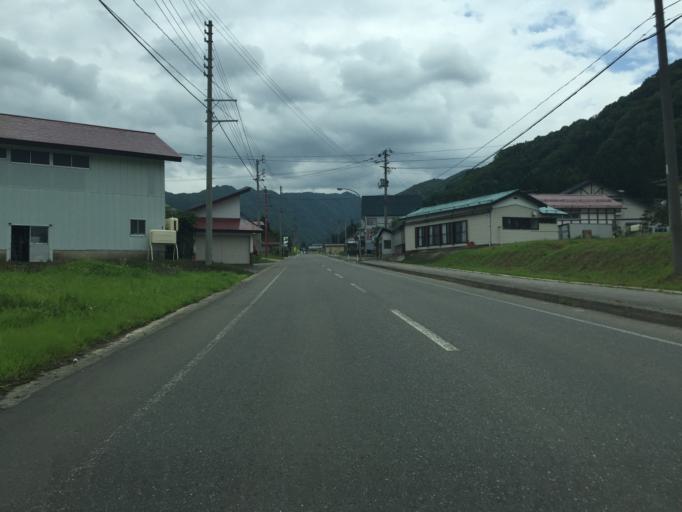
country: JP
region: Yamagata
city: Yonezawa
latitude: 37.8331
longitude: 140.0953
